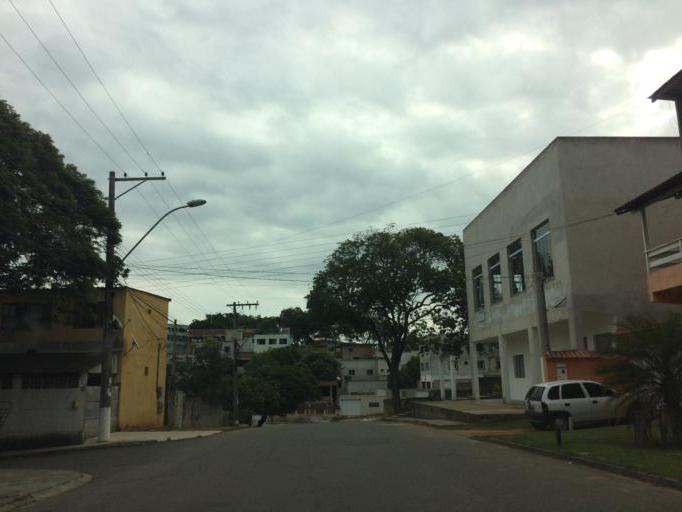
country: BR
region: Espirito Santo
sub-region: Guarapari
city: Guarapari
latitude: -20.6551
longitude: -40.5069
